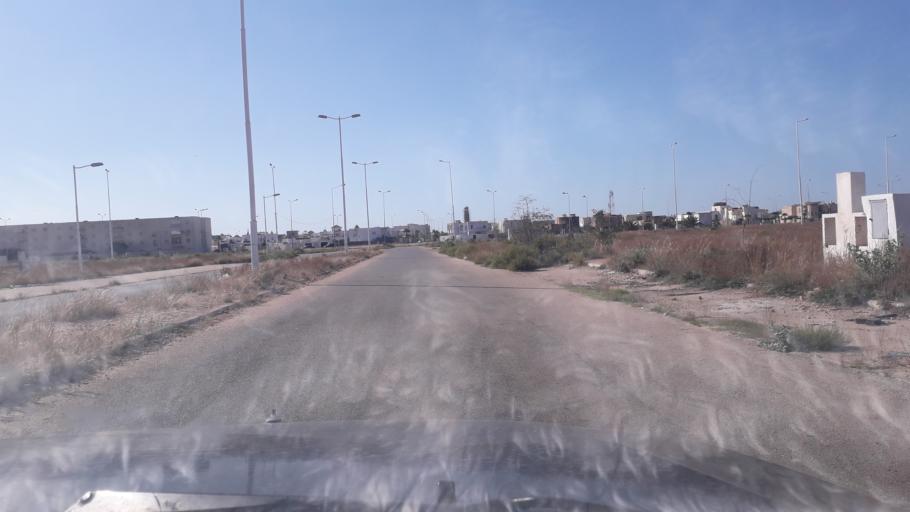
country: TN
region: Safaqis
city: Al Qarmadah
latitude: 34.8332
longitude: 10.7546
